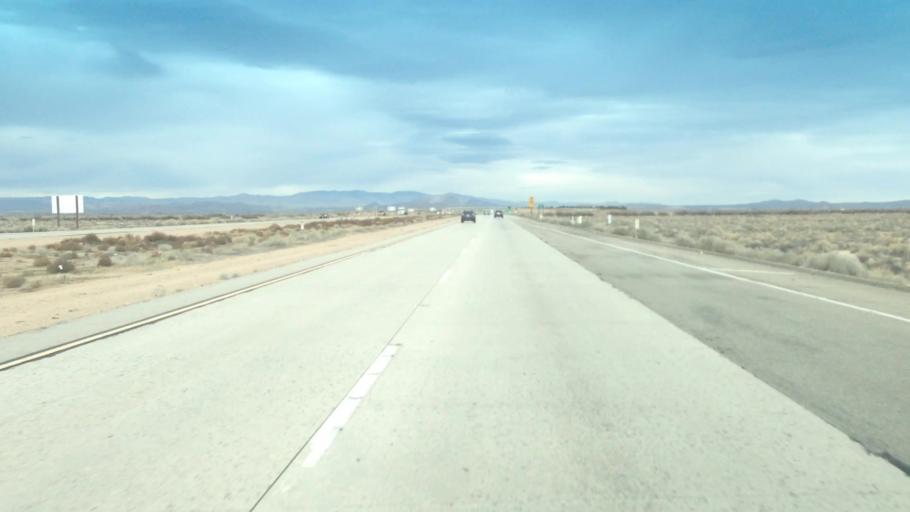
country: US
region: California
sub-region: Los Angeles County
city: Lancaster
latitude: 34.7355
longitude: -118.1698
